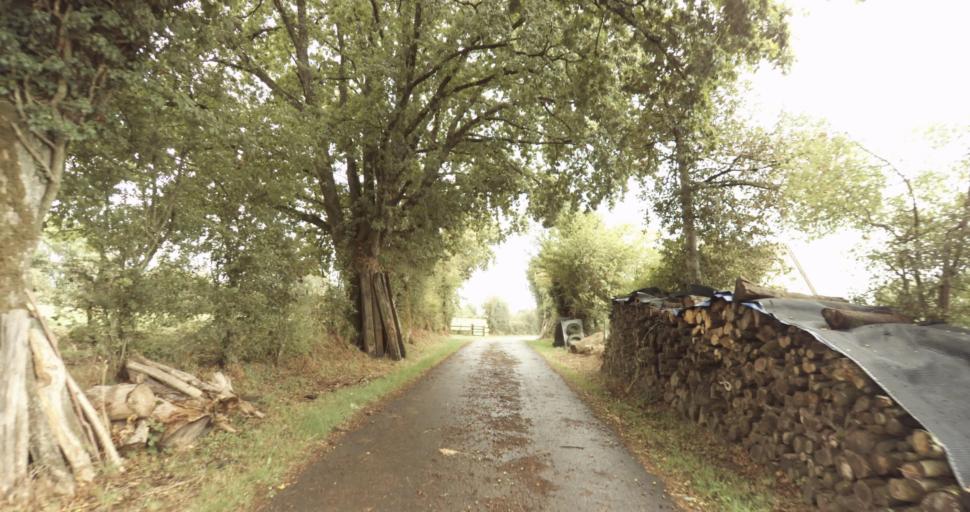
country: FR
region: Lower Normandy
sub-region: Departement de l'Orne
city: Sainte-Gauburge-Sainte-Colombe
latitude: 48.7186
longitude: 0.3830
